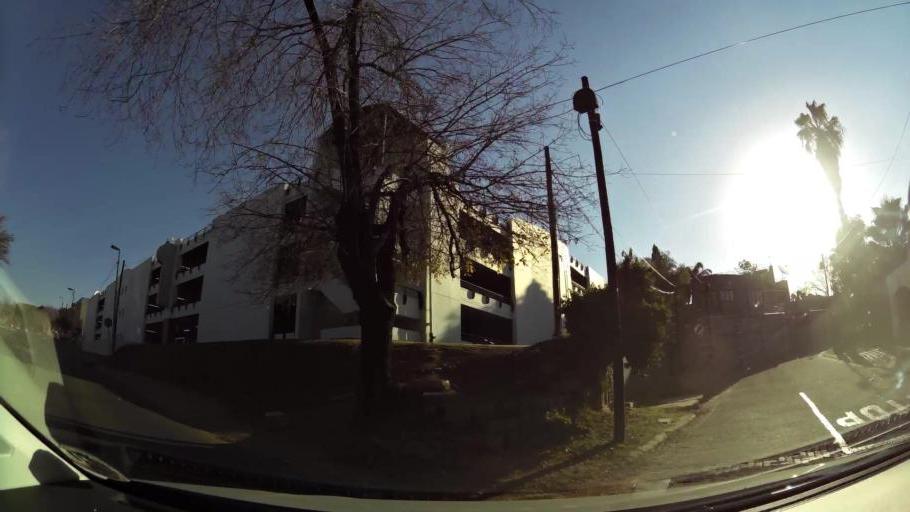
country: ZA
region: Gauteng
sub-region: City of Johannesburg Metropolitan Municipality
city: Modderfontein
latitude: -26.0993
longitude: 28.0673
